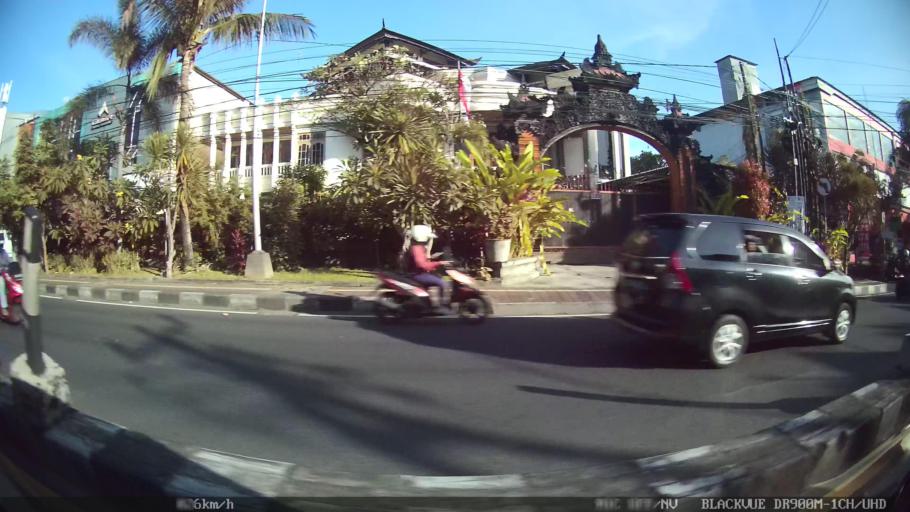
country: ID
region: Bali
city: Denpasar
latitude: -8.6367
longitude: 115.2165
